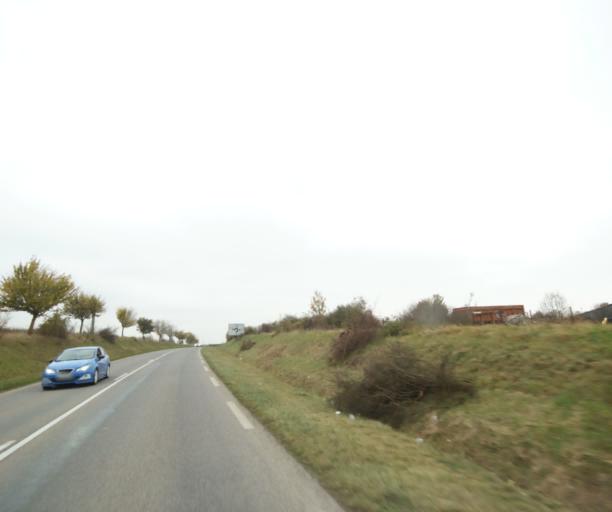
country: FR
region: Lorraine
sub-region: Departement de Meurthe-et-Moselle
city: Briey
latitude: 49.2520
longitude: 5.9524
